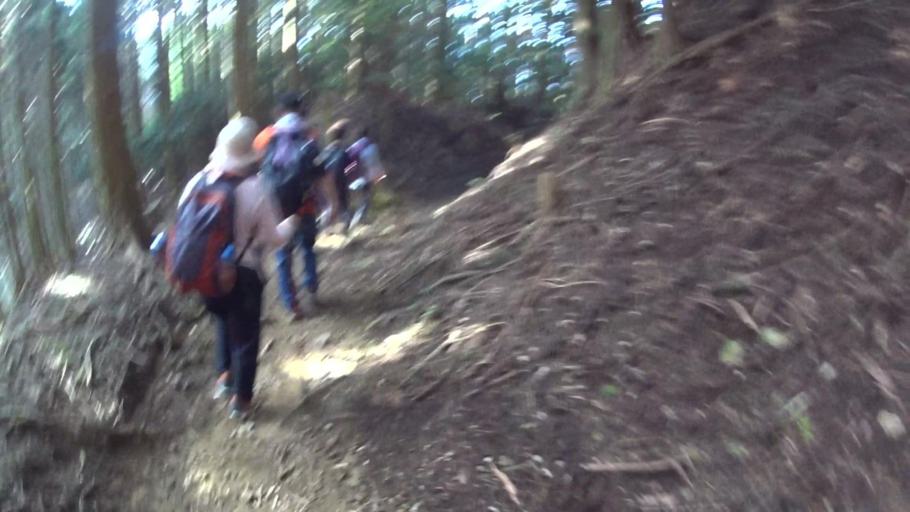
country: JP
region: Shiga Prefecture
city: Kitahama
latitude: 35.1064
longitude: 135.8429
